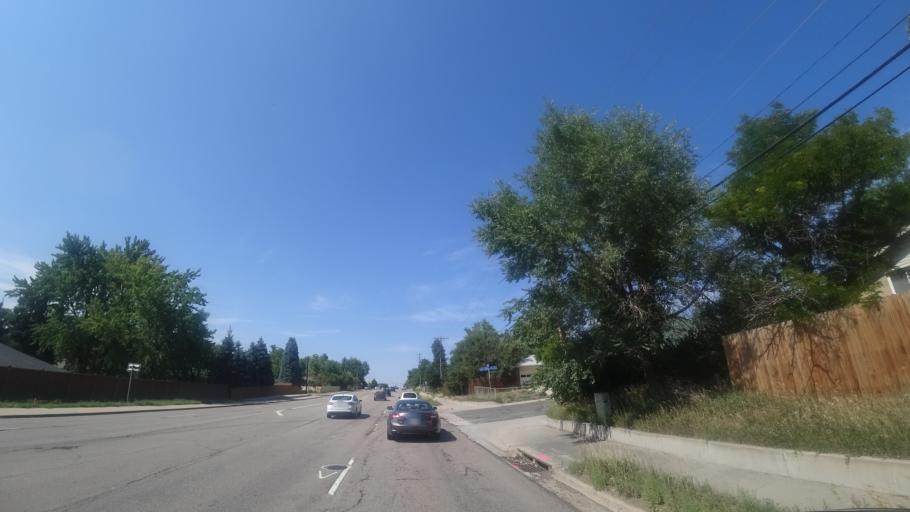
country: US
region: Colorado
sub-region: Arapahoe County
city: Greenwood Village
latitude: 39.6060
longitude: -104.9600
